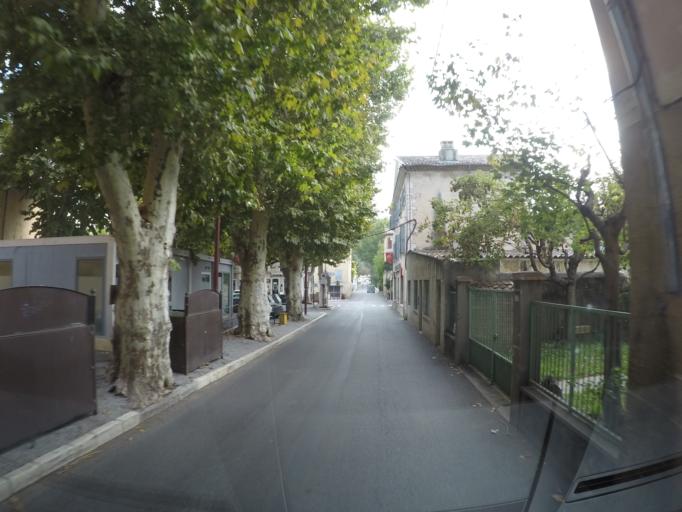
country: FR
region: Provence-Alpes-Cote d'Azur
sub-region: Departement des Alpes-de-Haute-Provence
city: Riez
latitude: 43.8184
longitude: 6.0906
